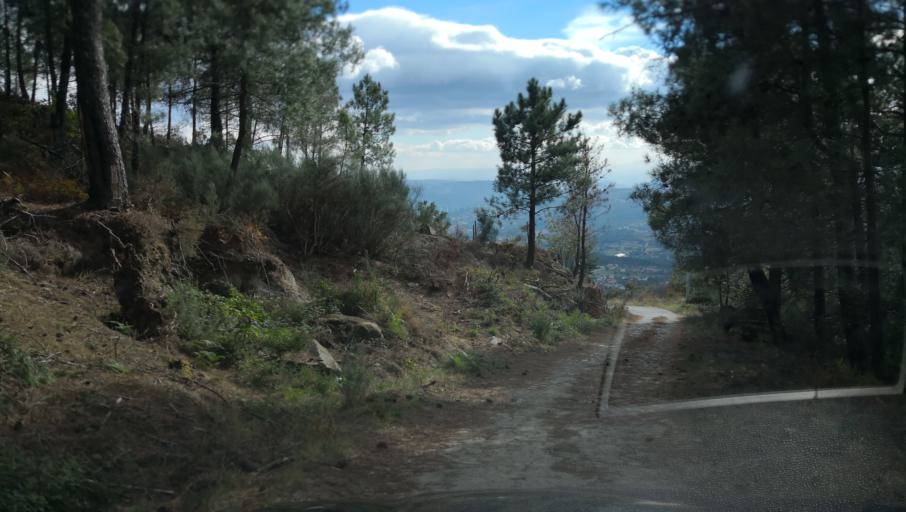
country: PT
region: Vila Real
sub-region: Vila Real
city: Vila Real
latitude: 41.3343
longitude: -7.7708
